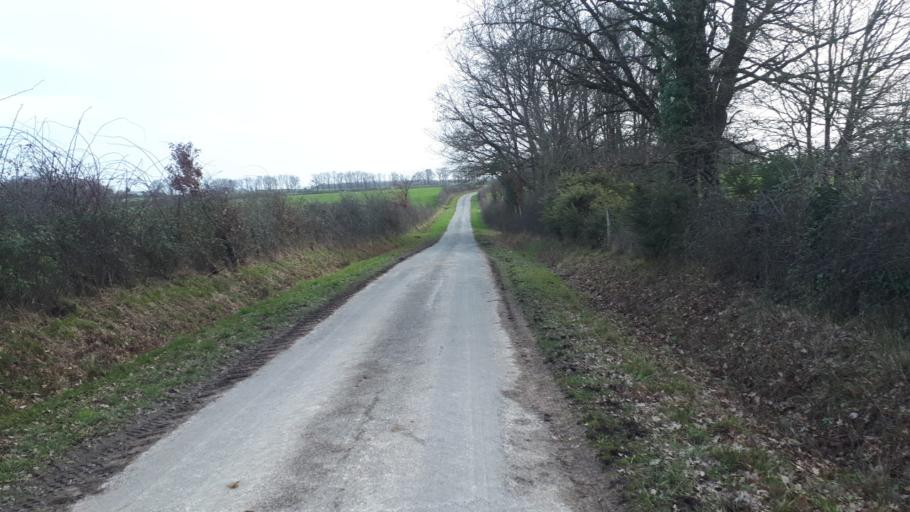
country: FR
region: Poitou-Charentes
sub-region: Departement de la Vienne
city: Archigny
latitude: 46.6244
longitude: 0.7456
